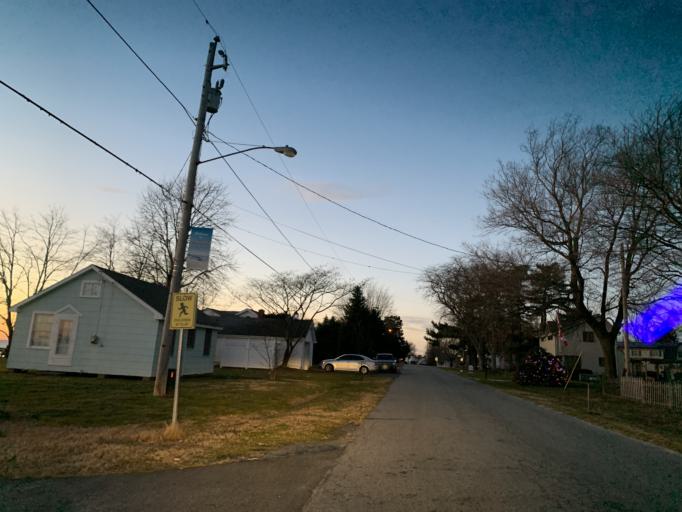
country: US
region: Maryland
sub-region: Kent County
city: Rock Hall
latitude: 39.1378
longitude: -76.2569
